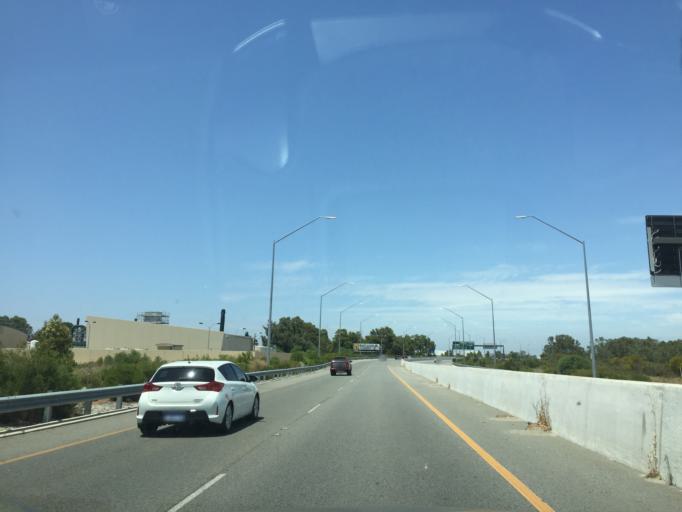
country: AU
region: Western Australia
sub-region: Belmont
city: Kewdale
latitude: -31.9588
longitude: 115.9681
